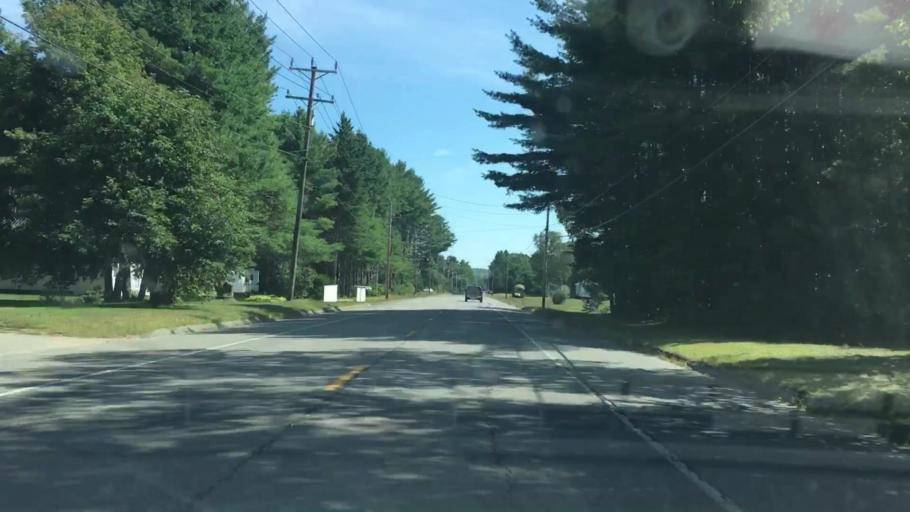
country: US
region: Maine
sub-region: Piscataquis County
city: Milo
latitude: 45.2402
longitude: -68.9688
